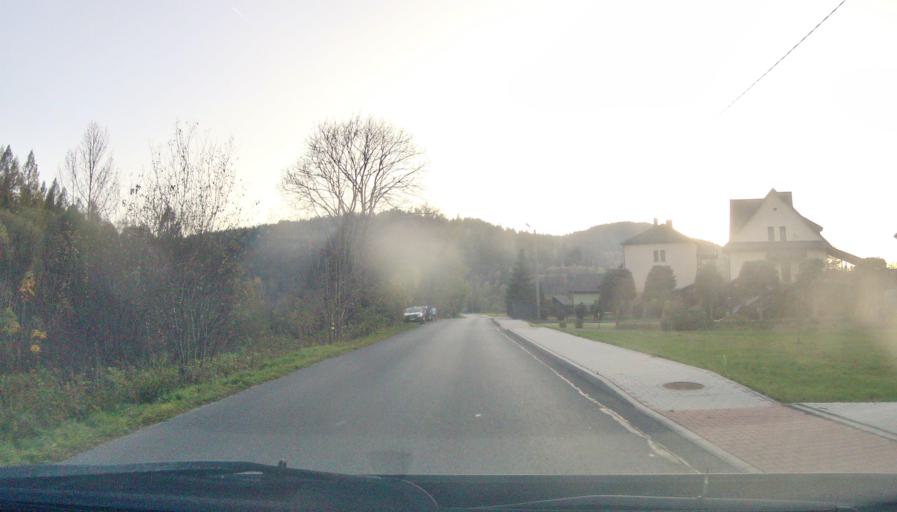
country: PL
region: Lesser Poland Voivodeship
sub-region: Powiat suski
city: Kukow
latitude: 49.7428
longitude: 19.4653
